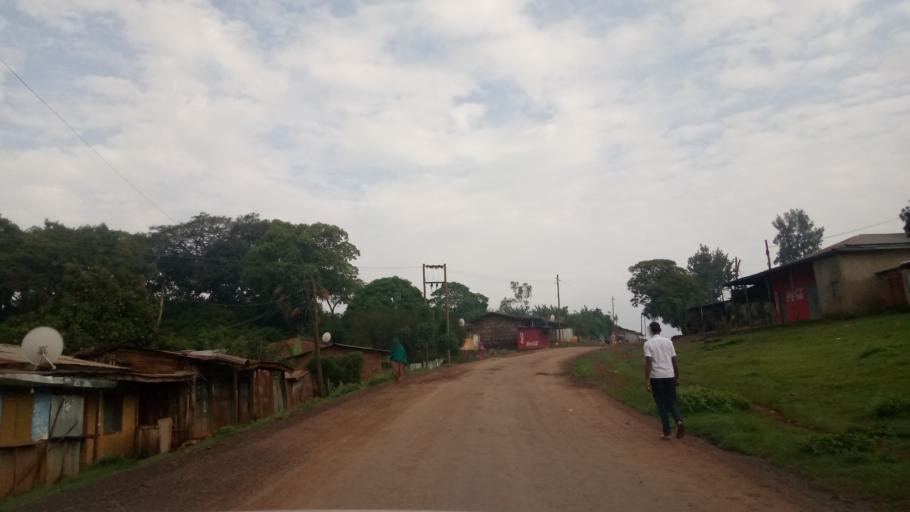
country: ET
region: Oromiya
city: Agaro
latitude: 7.8357
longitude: 36.6725
